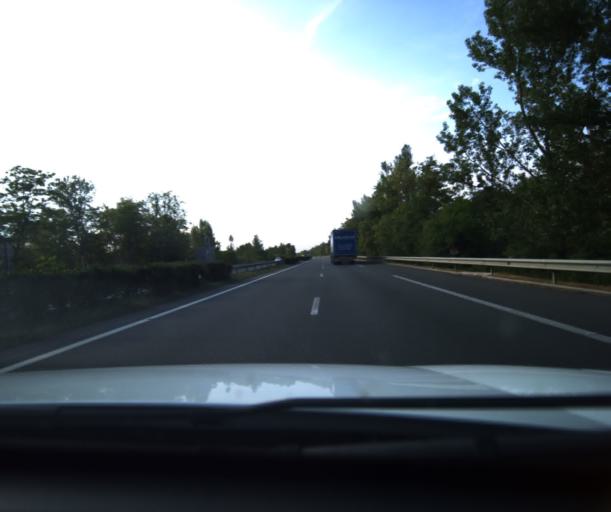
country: FR
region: Midi-Pyrenees
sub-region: Departement du Tarn-et-Garonne
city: Bressols
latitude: 43.9470
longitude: 1.2928
